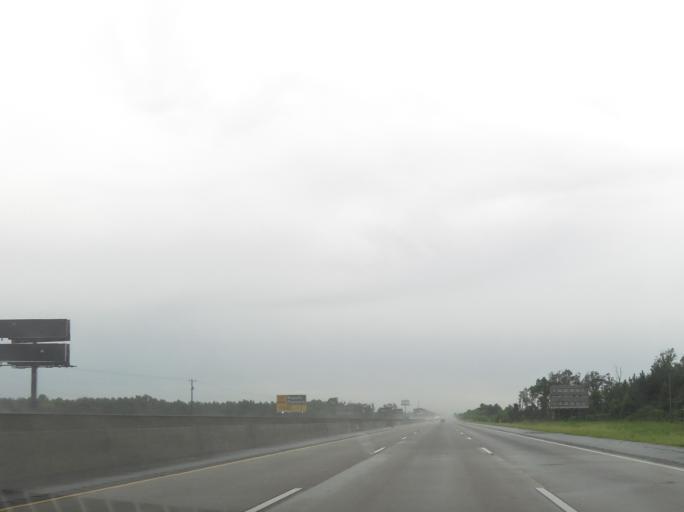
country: US
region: Georgia
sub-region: Tift County
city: Unionville
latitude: 31.3913
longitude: -83.4985
